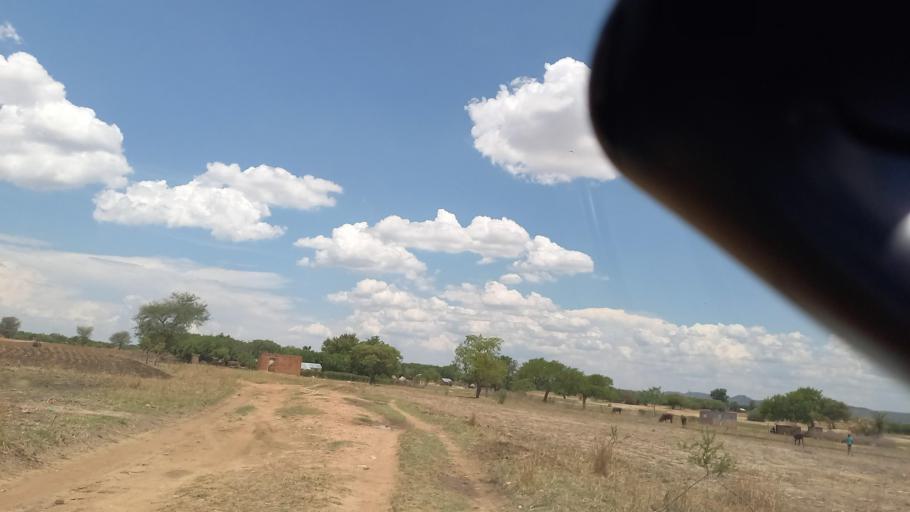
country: ZM
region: Southern
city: Mazabuka
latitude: -16.1147
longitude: 27.8127
